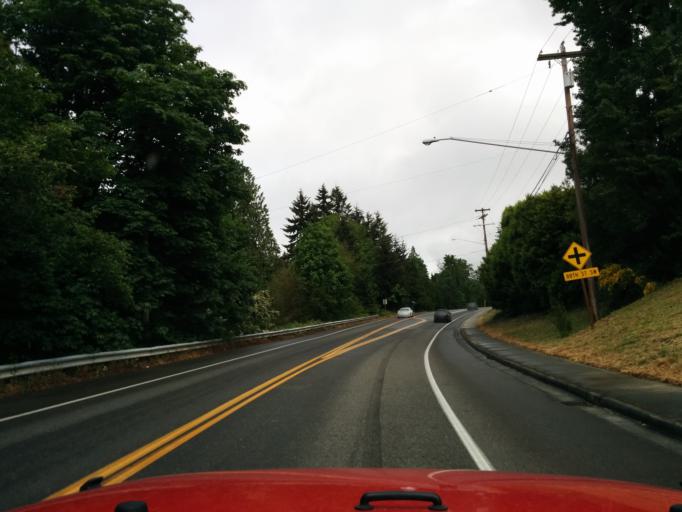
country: US
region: Washington
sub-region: Snohomish County
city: Mukilteo
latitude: 47.9171
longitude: -122.2996
